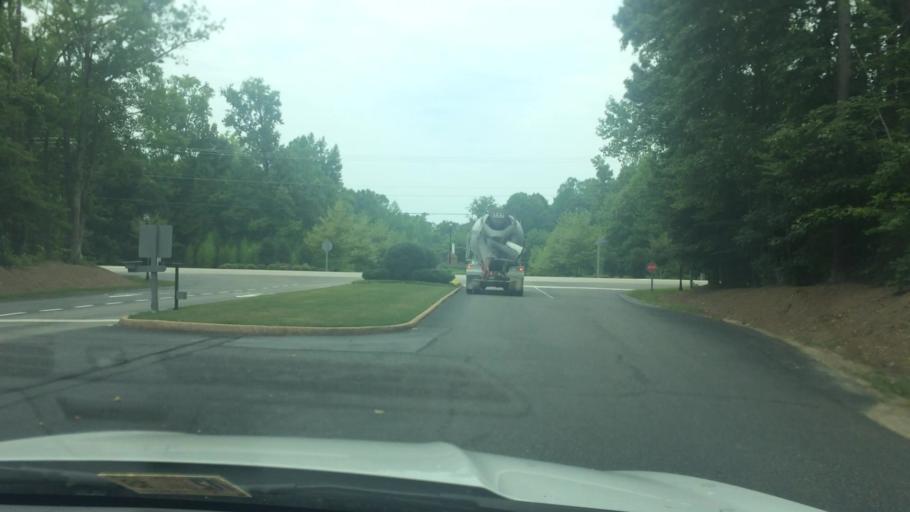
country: US
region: Virginia
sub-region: James City County
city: Williamsburg
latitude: 37.2933
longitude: -76.7984
